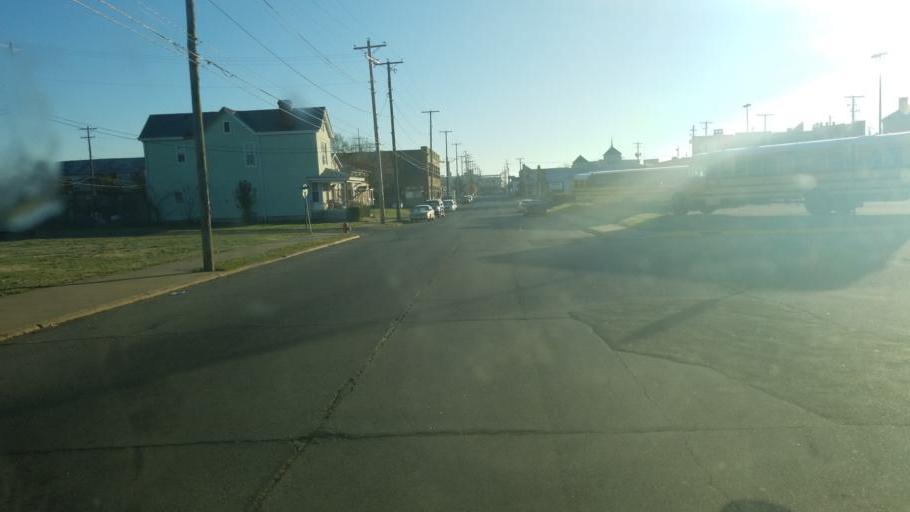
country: US
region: Ohio
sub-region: Scioto County
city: Portsmouth
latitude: 38.7371
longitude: -82.9883
